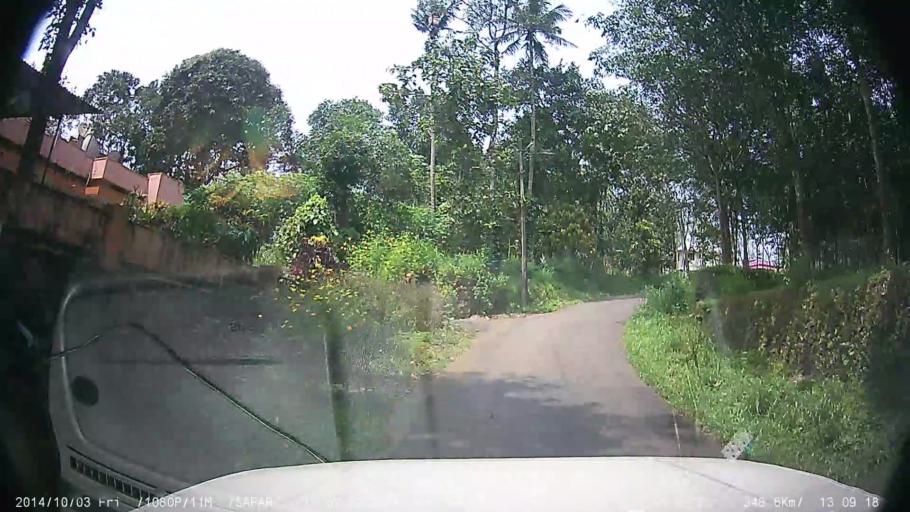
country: IN
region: Kerala
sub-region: Kottayam
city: Palackattumala
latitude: 9.7817
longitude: 76.5606
